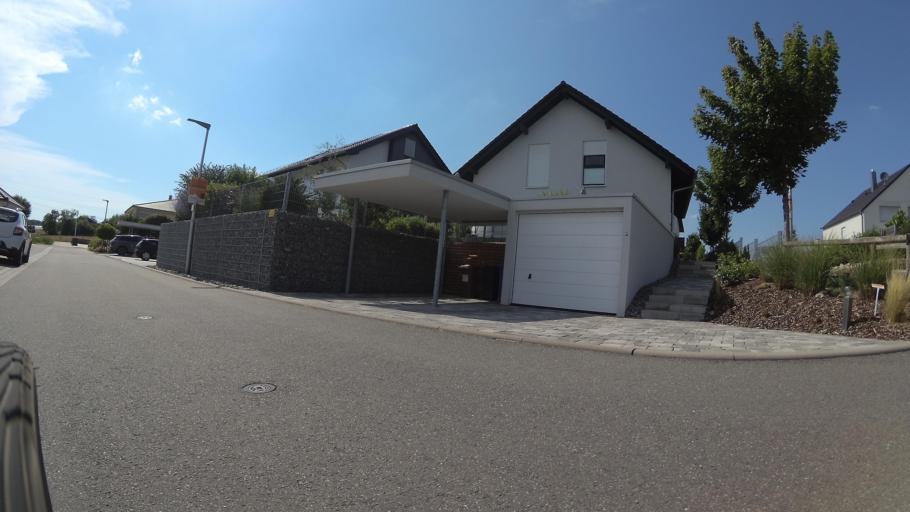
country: DE
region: Baden-Wuerttemberg
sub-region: Regierungsbezirk Stuttgart
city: Bad Wimpfen
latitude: 49.2426
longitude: 9.1338
